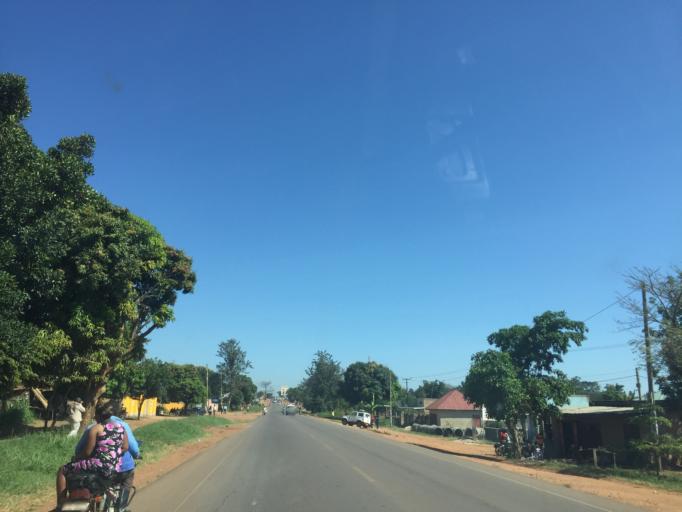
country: UG
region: Central Region
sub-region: Luwero District
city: Luwero
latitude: 0.8224
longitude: 32.5029
